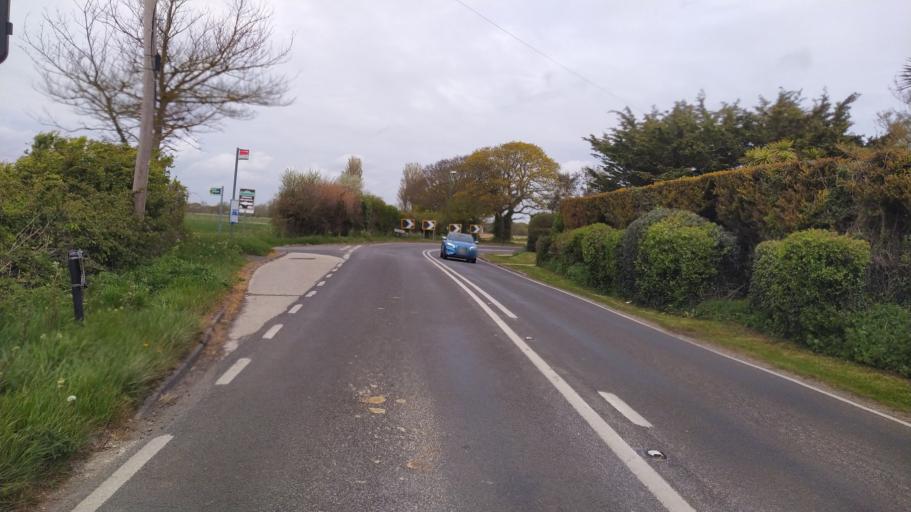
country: GB
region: England
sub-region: West Sussex
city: Birdham
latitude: 50.7781
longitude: -0.8475
